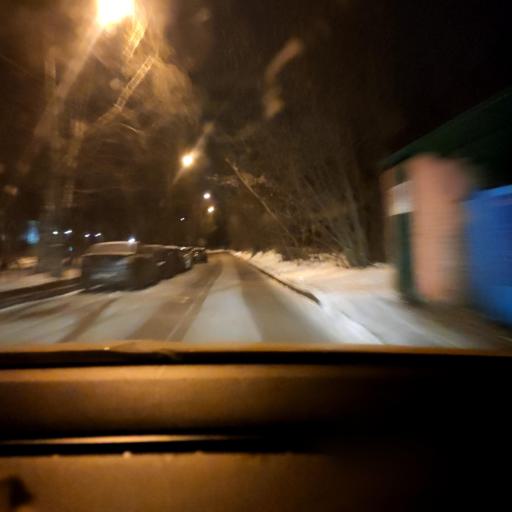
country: RU
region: Moscow
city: Metrogorodok
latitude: 55.8290
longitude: 37.7645
